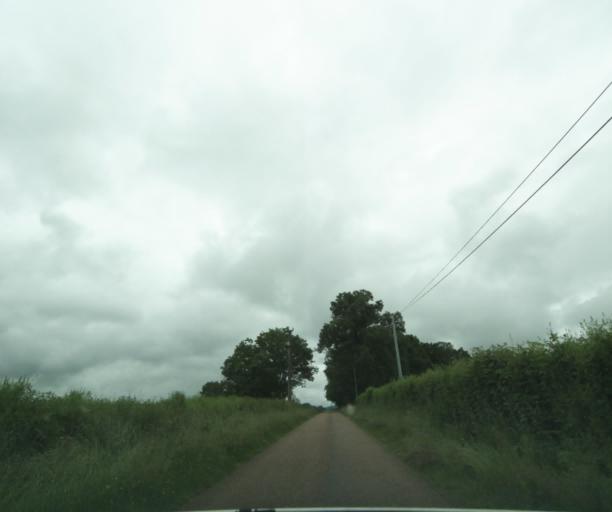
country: FR
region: Bourgogne
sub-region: Departement de Saone-et-Loire
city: Charolles
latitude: 46.4658
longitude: 4.3505
